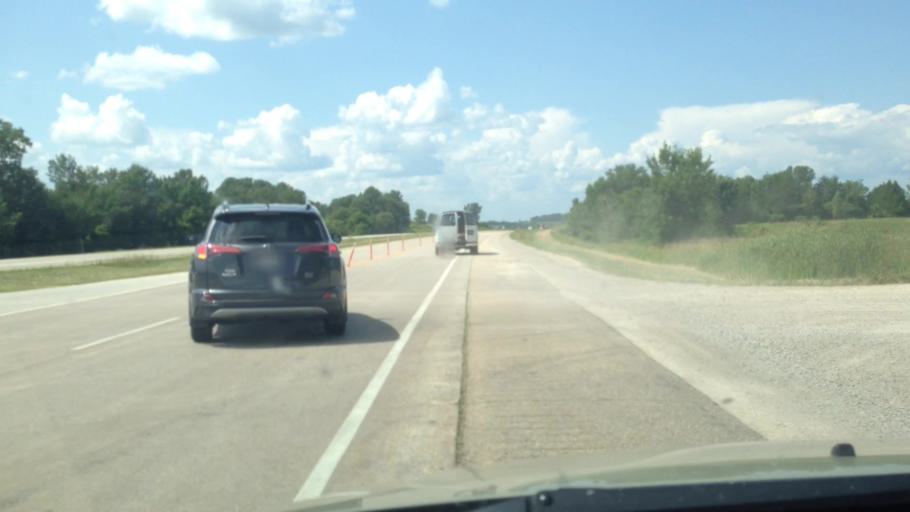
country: US
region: Wisconsin
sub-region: Shawano County
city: Bonduel
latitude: 44.7054
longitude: -88.3743
